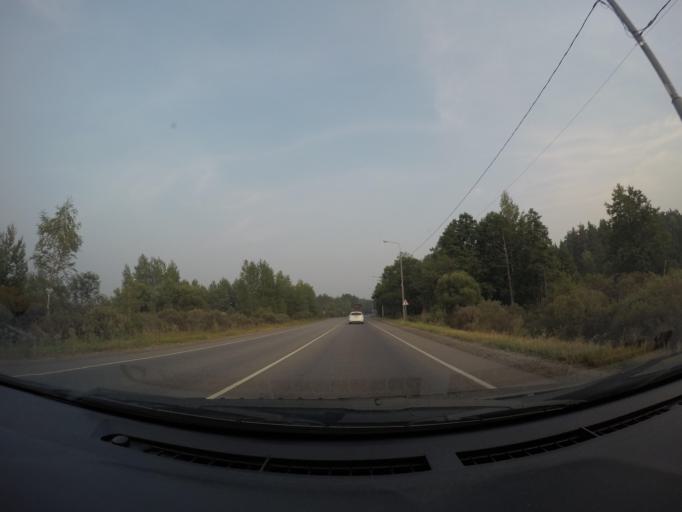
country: RU
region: Moskovskaya
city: Imeni Tsyurupy
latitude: 55.5165
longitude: 38.7213
